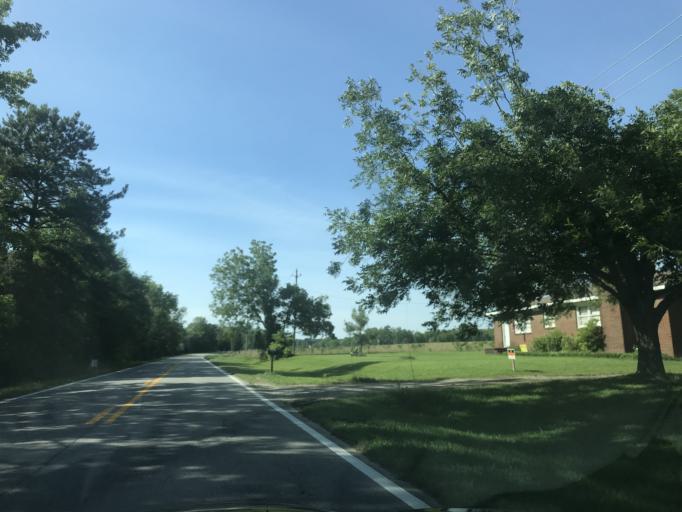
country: US
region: North Carolina
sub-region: Johnston County
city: Clayton
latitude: 35.6095
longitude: -78.5348
